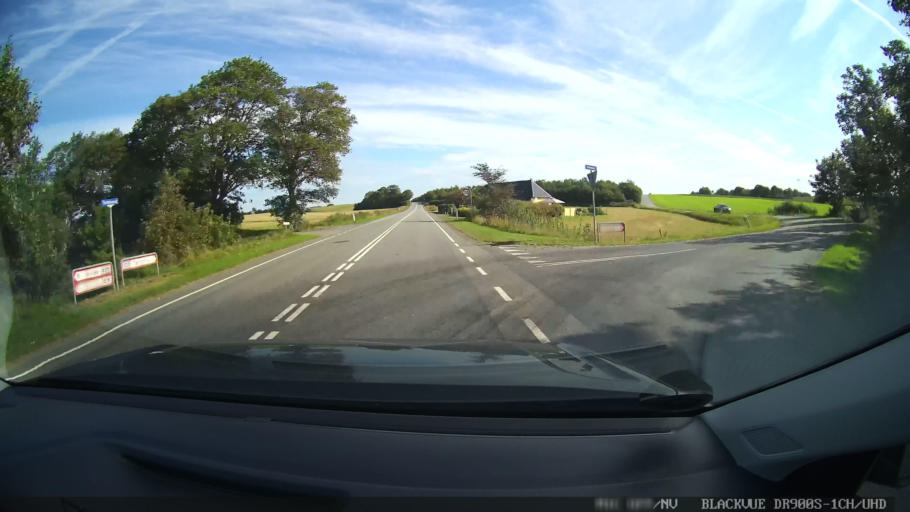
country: DK
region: North Denmark
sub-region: Mariagerfjord Kommune
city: Hadsund
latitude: 56.7767
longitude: 10.0057
